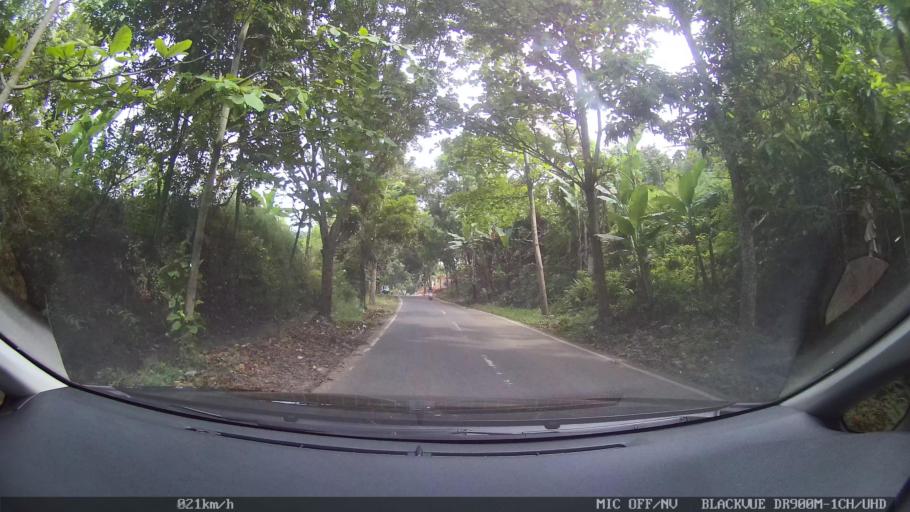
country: ID
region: Lampung
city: Bandarlampung
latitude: -5.4440
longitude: 105.2420
